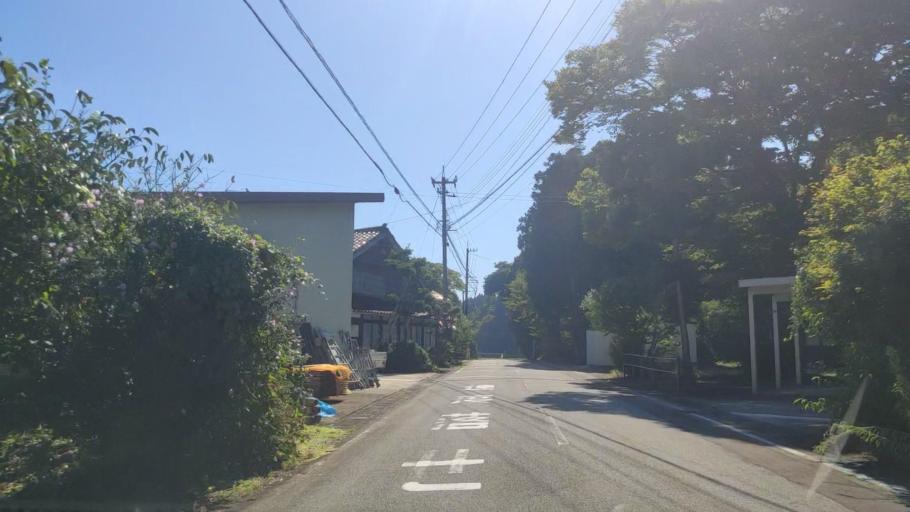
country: JP
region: Toyama
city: Nyuzen
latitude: 37.4807
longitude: 137.3374
